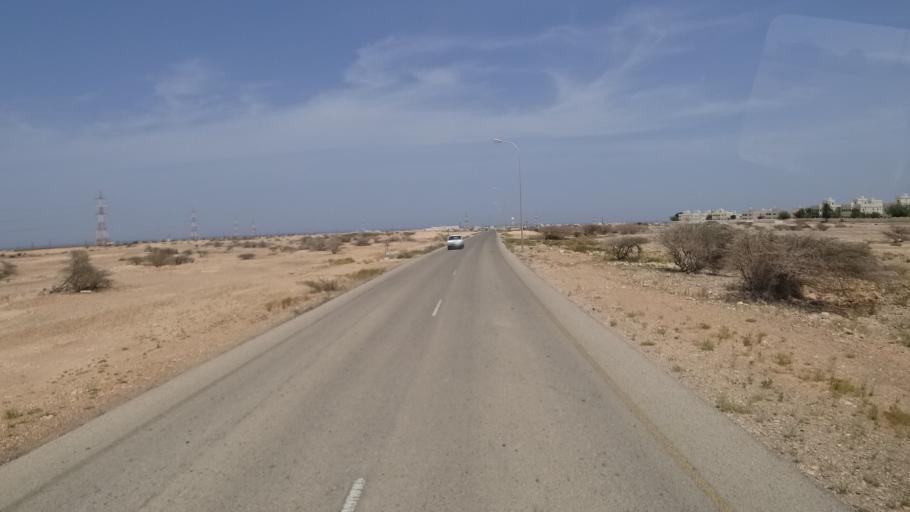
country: OM
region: Ash Sharqiyah
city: Sur
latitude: 22.6112
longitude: 59.4381
